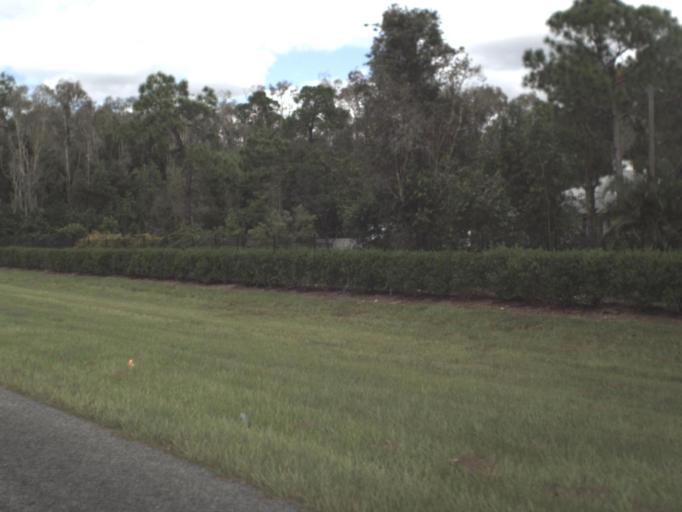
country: US
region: Florida
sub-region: Lee County
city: Villas
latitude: 26.5089
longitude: -81.8517
